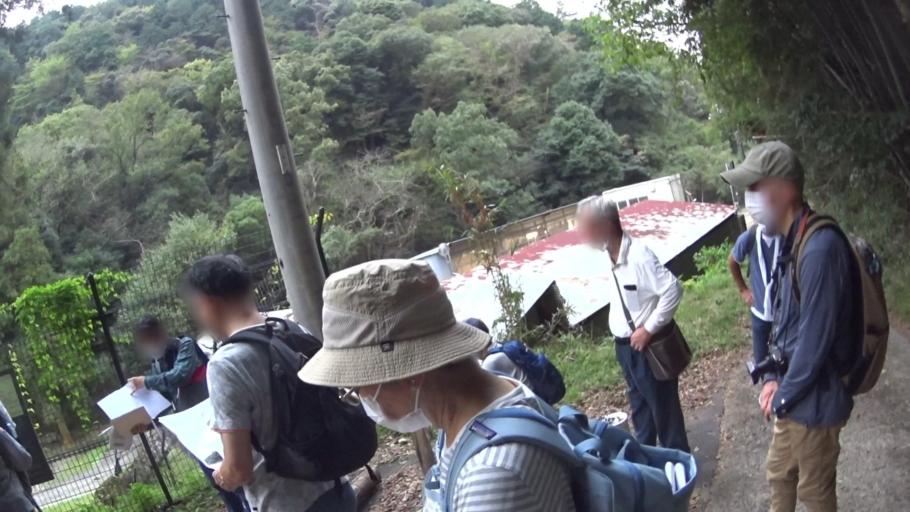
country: JP
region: Gifu
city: Tarui
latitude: 35.2953
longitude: 136.4237
